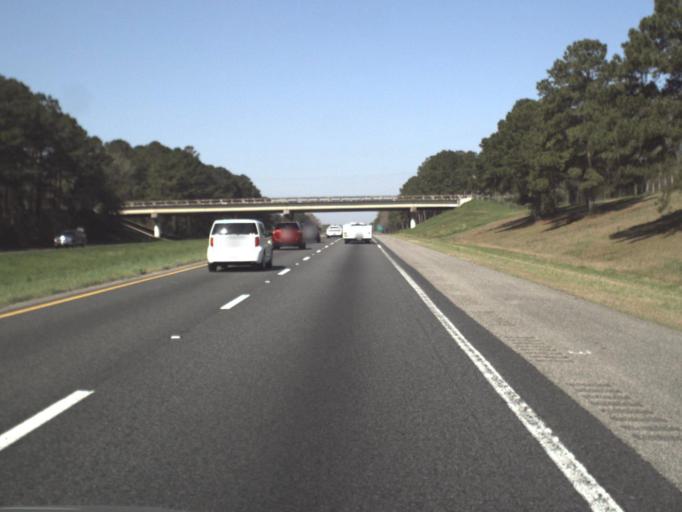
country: US
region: Florida
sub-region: Gadsden County
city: Gretna
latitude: 30.5700
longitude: -84.6712
